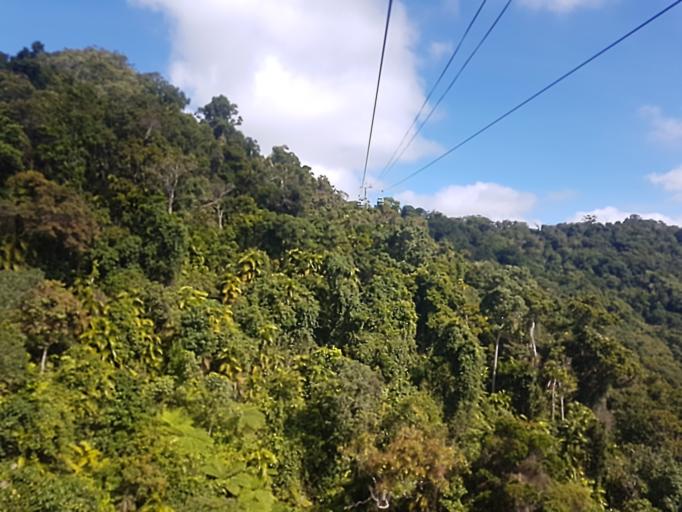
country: AU
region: Queensland
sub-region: Cairns
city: Redlynch
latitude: -16.8490
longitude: 145.6753
